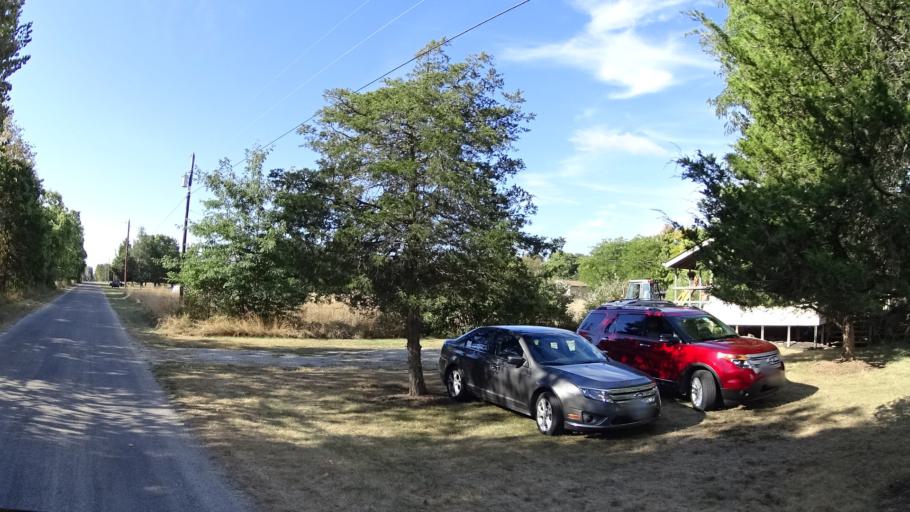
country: US
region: Ohio
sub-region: Erie County
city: Sandusky
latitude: 41.6106
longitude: -82.6887
